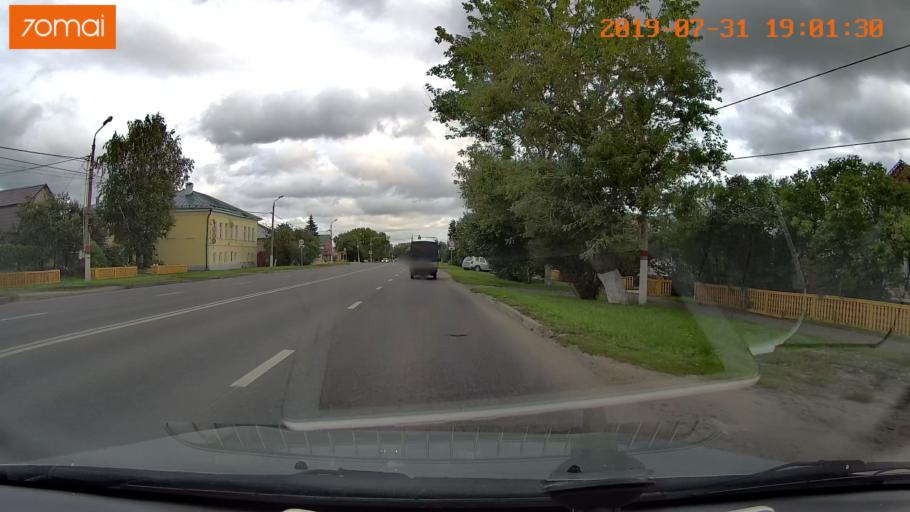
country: RU
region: Moskovskaya
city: Raduzhnyy
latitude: 55.1261
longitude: 38.7289
